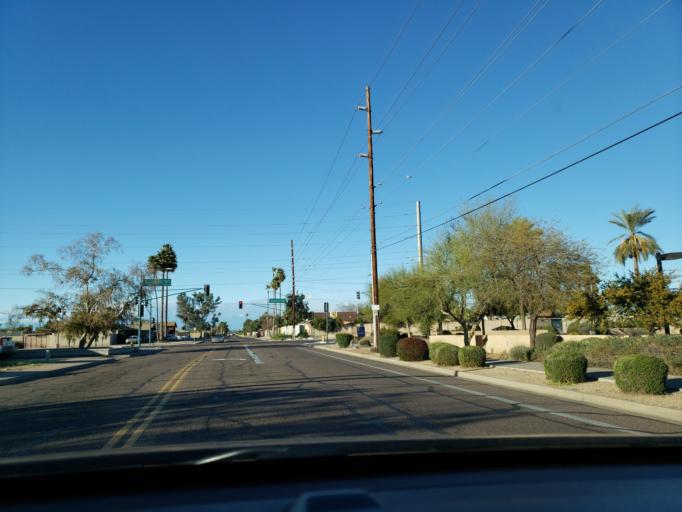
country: US
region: Arizona
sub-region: Maricopa County
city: Glendale
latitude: 33.6102
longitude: -112.1252
